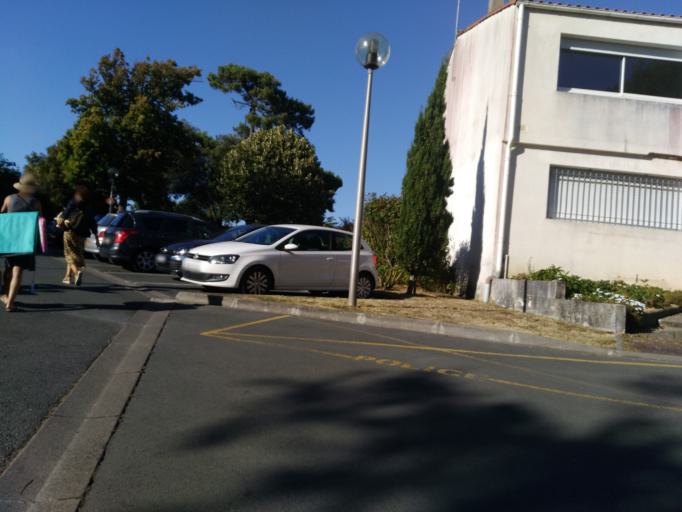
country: FR
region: Poitou-Charentes
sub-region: Departement de la Charente-Maritime
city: Saint-Palais-sur-Mer
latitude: 45.6428
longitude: -1.0854
